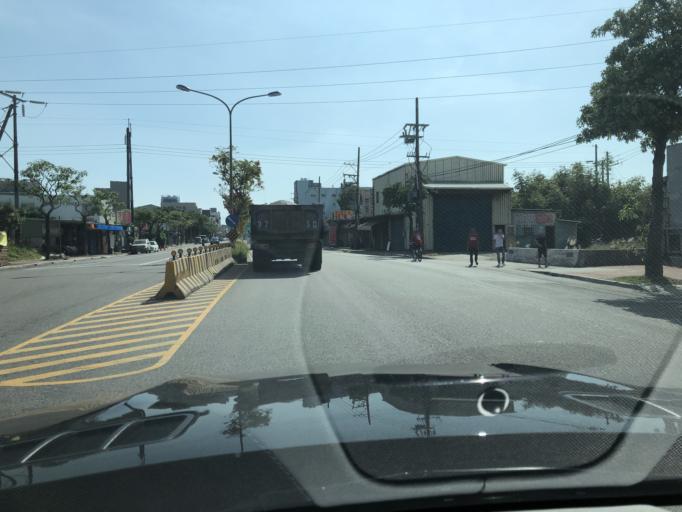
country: TW
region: Taiwan
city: Taoyuan City
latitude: 25.0759
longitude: 121.2853
